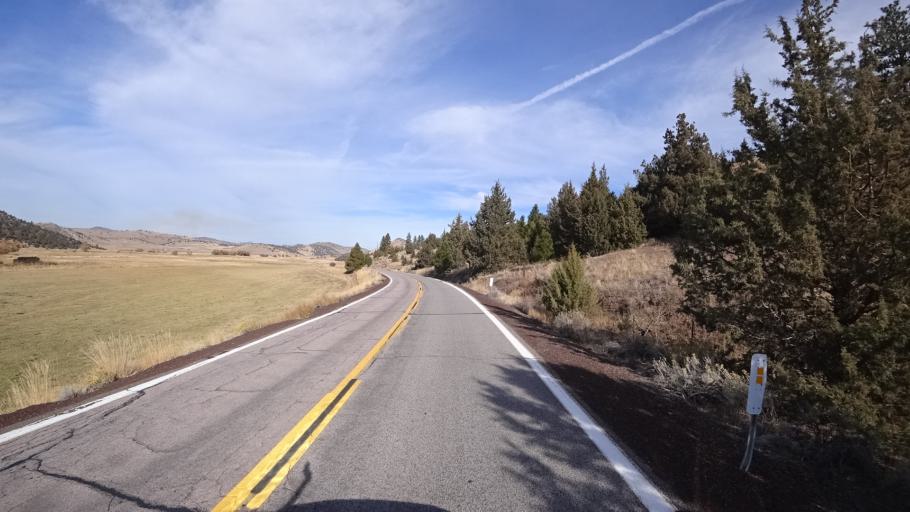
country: US
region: California
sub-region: Siskiyou County
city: Weed
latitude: 41.4766
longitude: -122.4113
